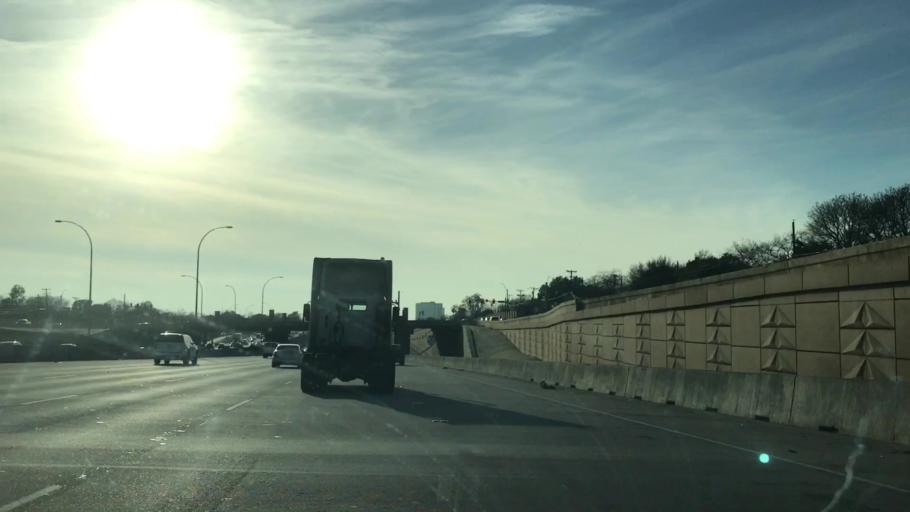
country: US
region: Texas
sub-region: Dallas County
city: Farmers Branch
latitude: 32.9193
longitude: -96.8539
